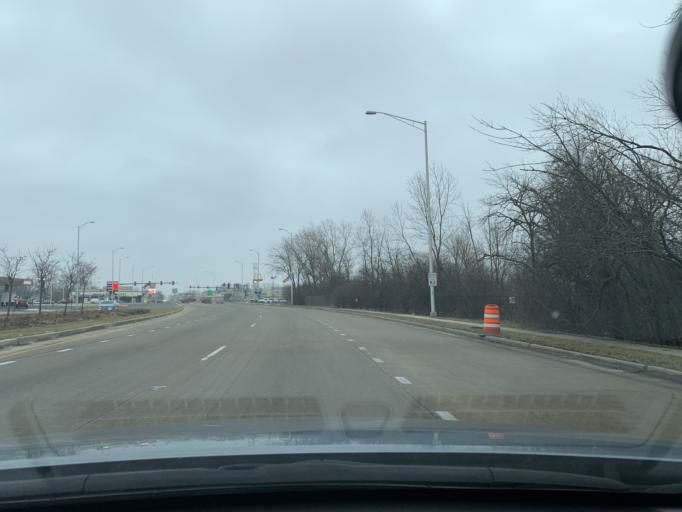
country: US
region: Illinois
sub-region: Cook County
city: Posen
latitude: 41.6228
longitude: -87.6773
